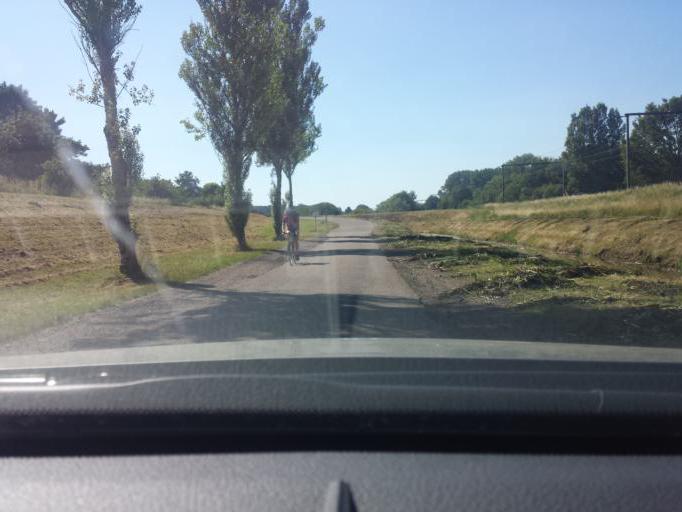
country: BE
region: Flanders
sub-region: Provincie Limburg
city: Herk-de-Stad
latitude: 50.9673
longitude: 5.1709
